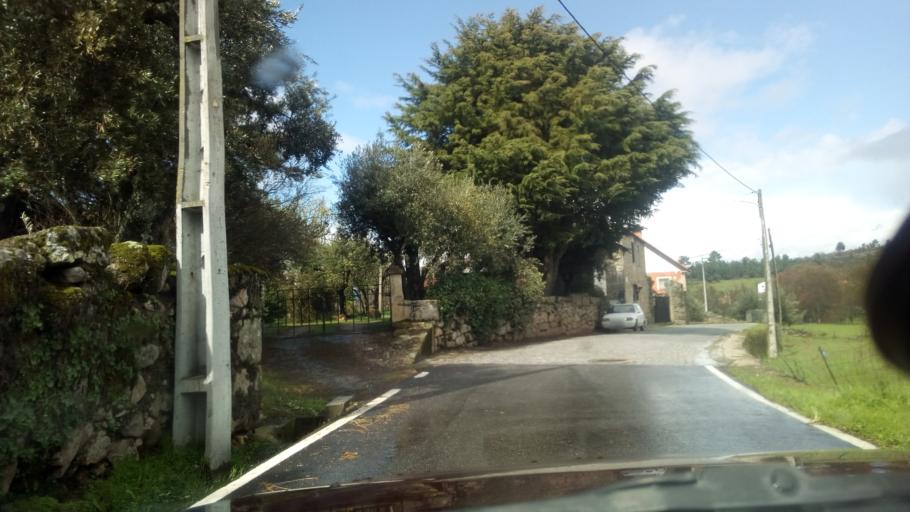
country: PT
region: Guarda
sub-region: Fornos de Algodres
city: Fornos de Algodres
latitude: 40.5792
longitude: -7.4716
